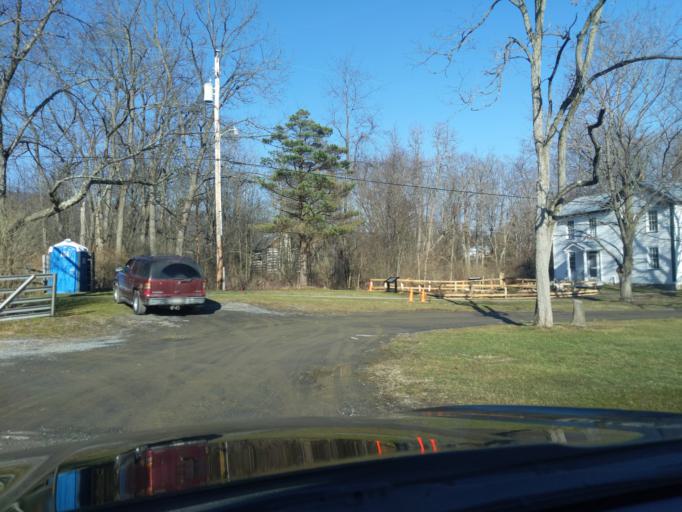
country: US
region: Pennsylvania
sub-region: Blair County
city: Bellwood
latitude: 40.5827
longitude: -78.2744
